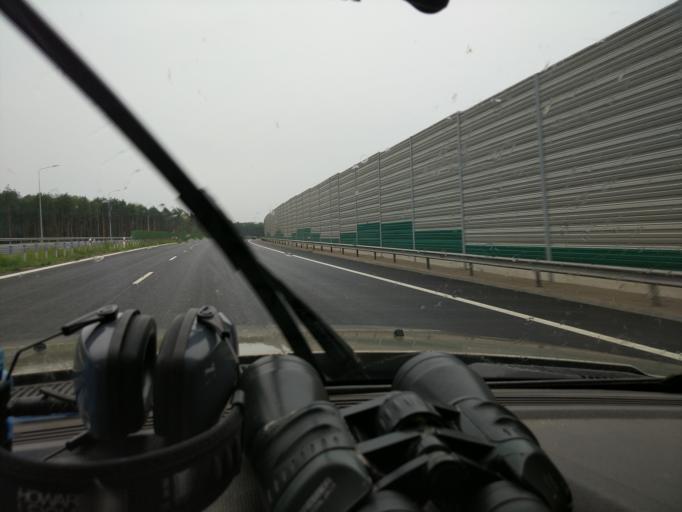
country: PL
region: Masovian Voivodeship
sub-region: Powiat wolominski
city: Slupno
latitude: 52.3760
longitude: 21.1883
